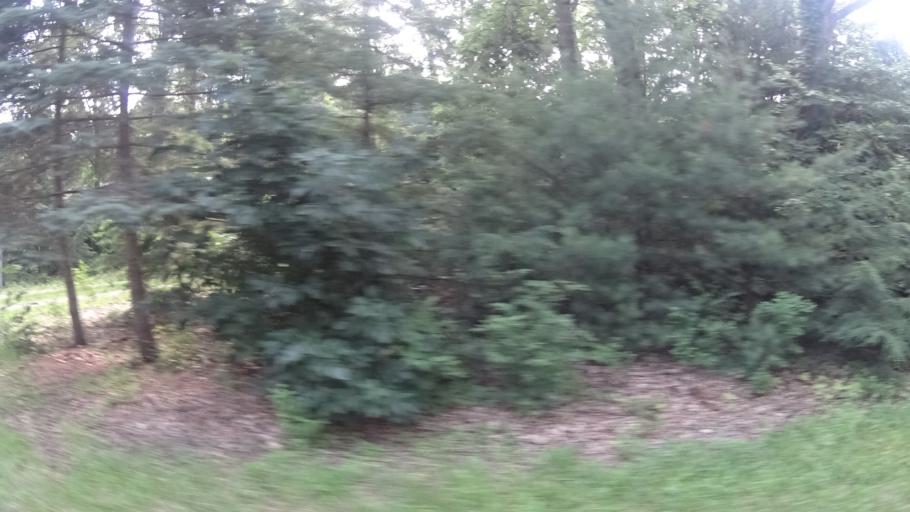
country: US
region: Ohio
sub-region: Lorain County
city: Vermilion
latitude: 41.3759
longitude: -82.4183
